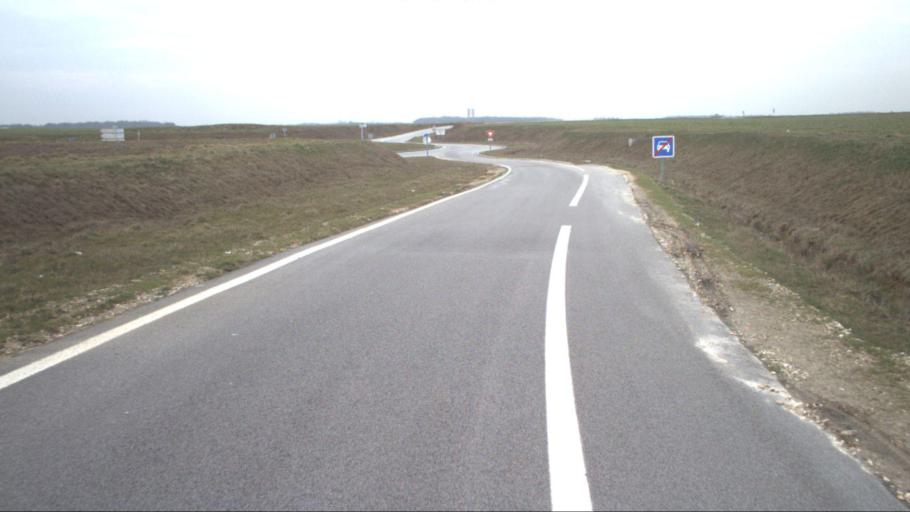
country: FR
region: Ile-de-France
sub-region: Departement des Yvelines
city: Sonchamp
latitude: 48.5798
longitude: 1.8315
